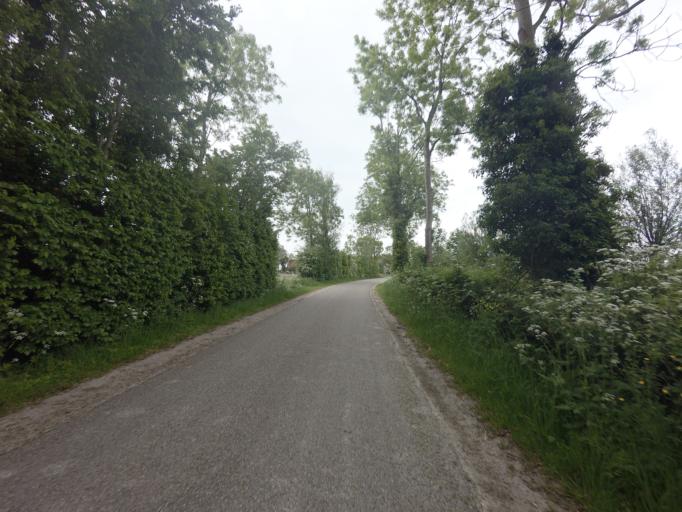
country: NL
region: Zeeland
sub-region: Gemeente Middelburg
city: Middelburg
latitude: 51.5280
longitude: 3.5708
